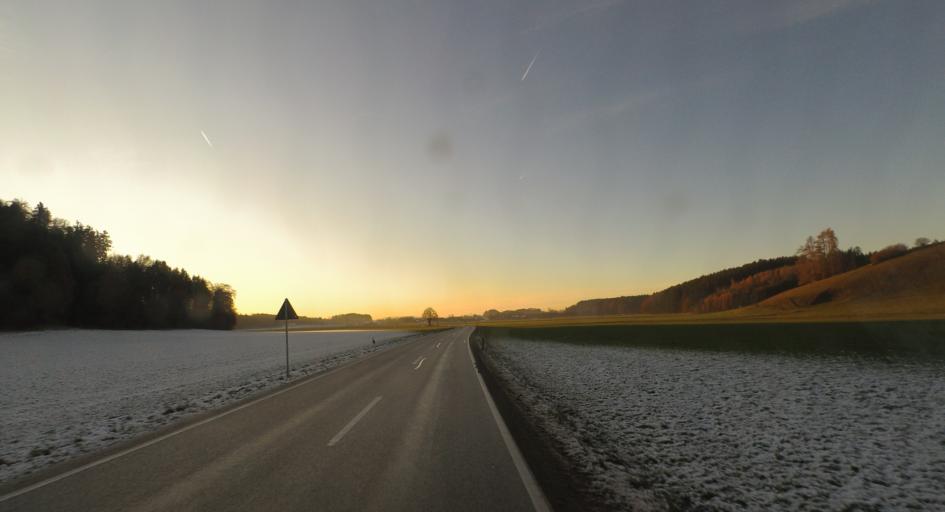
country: DE
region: Bavaria
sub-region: Upper Bavaria
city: Nussdorf
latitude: 47.8872
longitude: 12.5892
